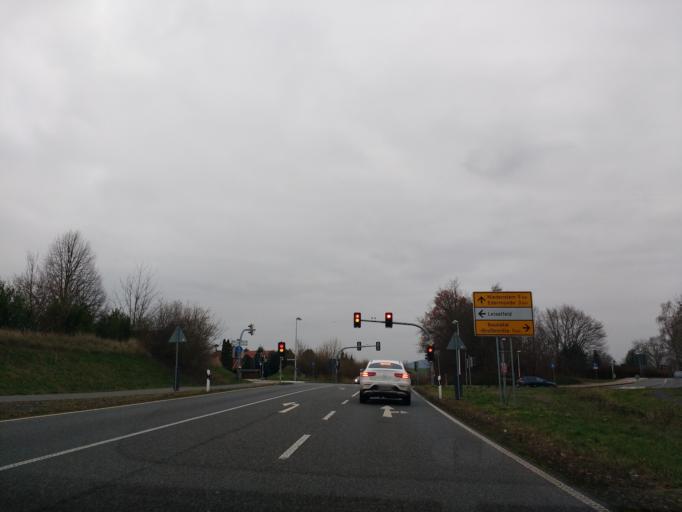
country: DE
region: Hesse
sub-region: Regierungsbezirk Kassel
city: Baunatal
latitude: 51.2499
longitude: 9.3978
